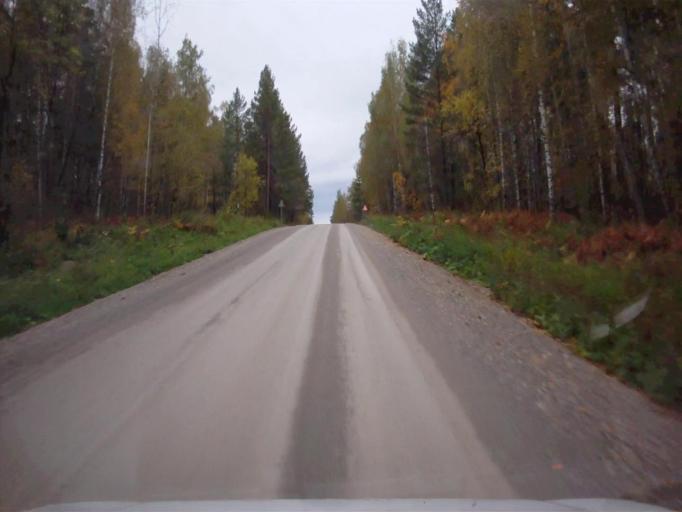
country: RU
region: Chelyabinsk
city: Nyazepetrovsk
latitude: 56.0700
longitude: 59.4314
